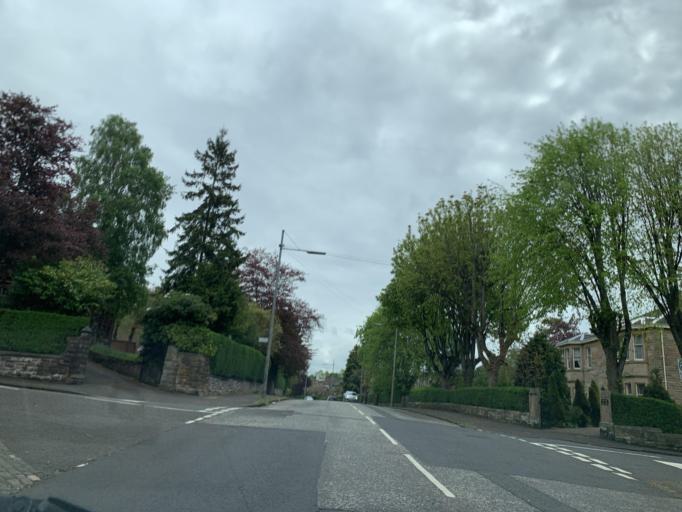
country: GB
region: Scotland
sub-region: East Renfrewshire
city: Giffnock
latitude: 55.8208
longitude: -4.2843
